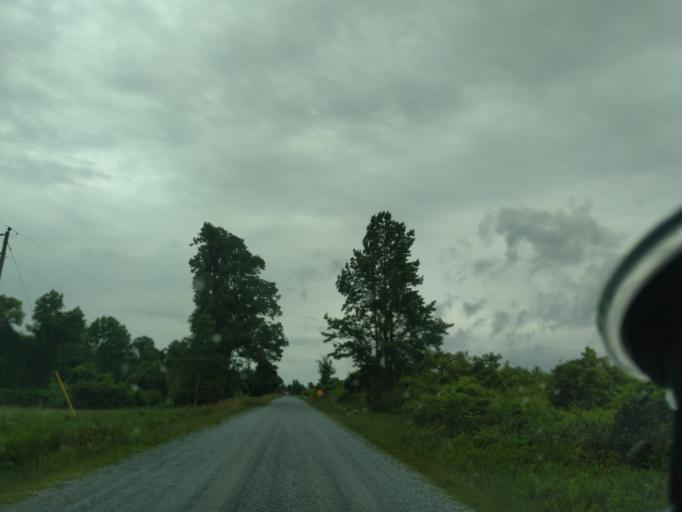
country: US
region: North Carolina
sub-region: Beaufort County
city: Belhaven
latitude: 35.7328
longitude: -76.4462
